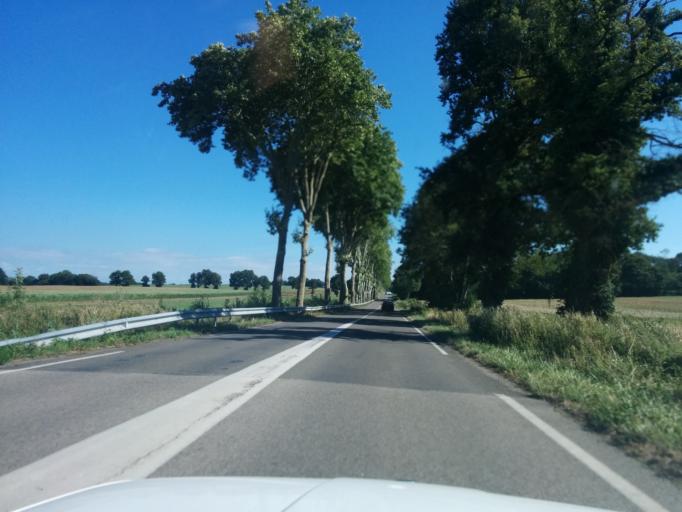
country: FR
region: Rhone-Alpes
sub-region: Departement de l'Ain
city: Perouges
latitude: 45.9380
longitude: 5.1806
